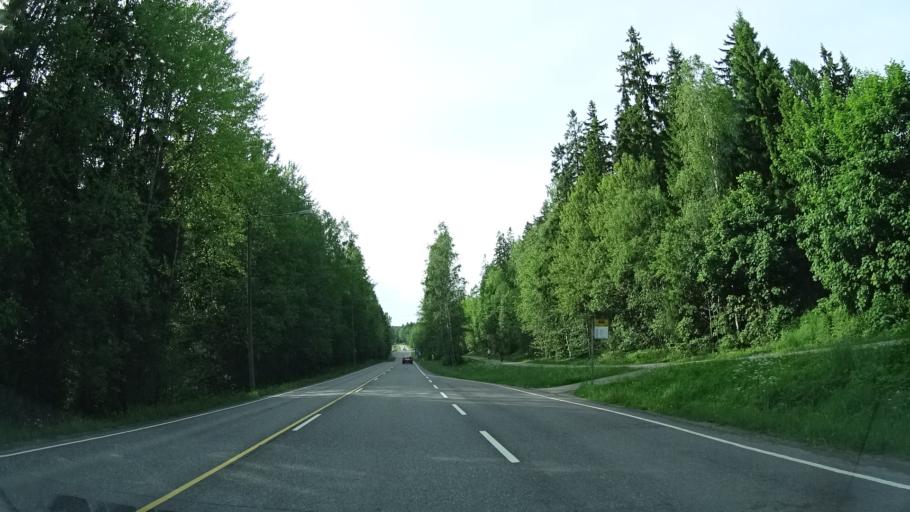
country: FI
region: Uusimaa
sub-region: Helsinki
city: Espoo
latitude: 60.2345
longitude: 24.6018
